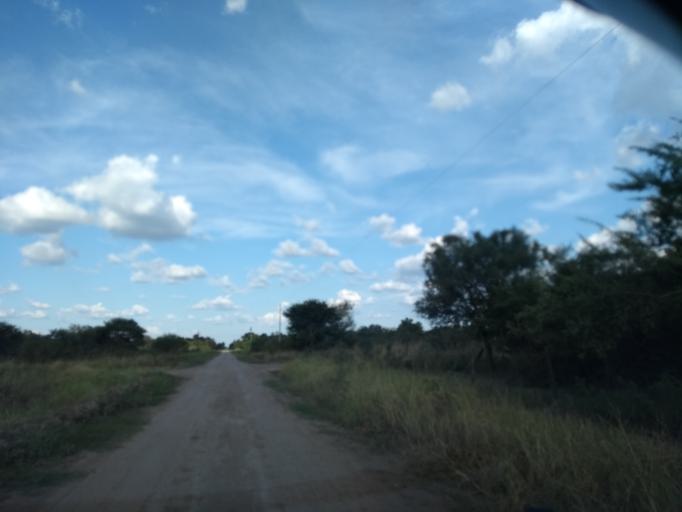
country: AR
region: Chaco
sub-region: Departamento de Quitilipi
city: Quitilipi
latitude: -26.7502
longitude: -60.2623
